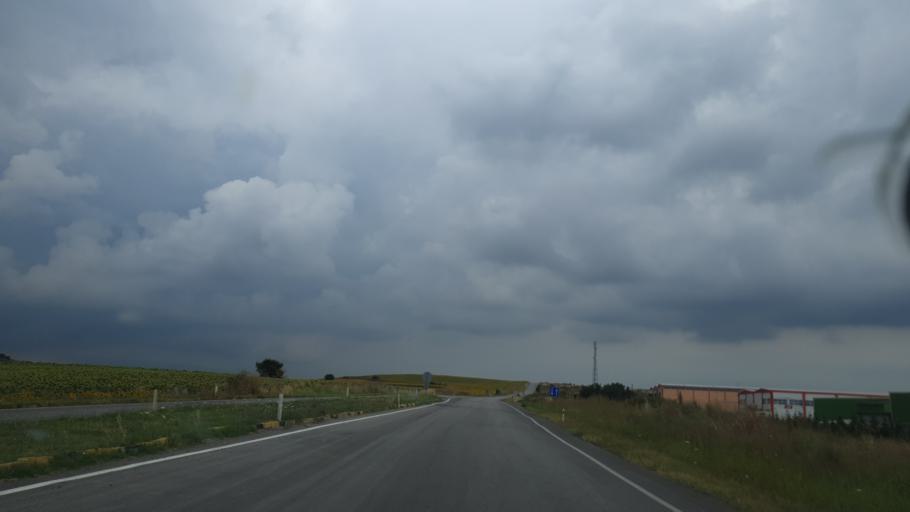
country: TR
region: Tekirdag
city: Hayrabolu
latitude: 41.2225
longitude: 27.0448
